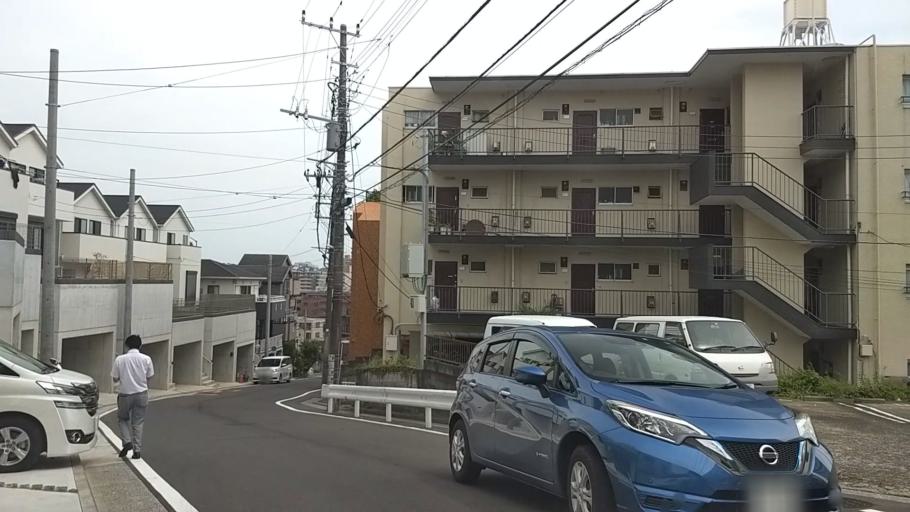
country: JP
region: Kanagawa
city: Yokohama
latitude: 35.4402
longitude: 139.6163
